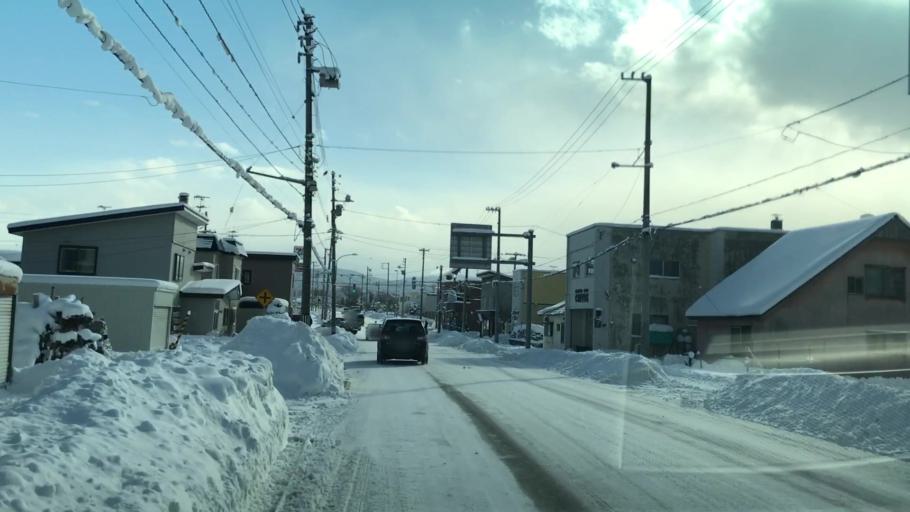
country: JP
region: Hokkaido
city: Yoichi
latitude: 43.1937
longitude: 140.7853
